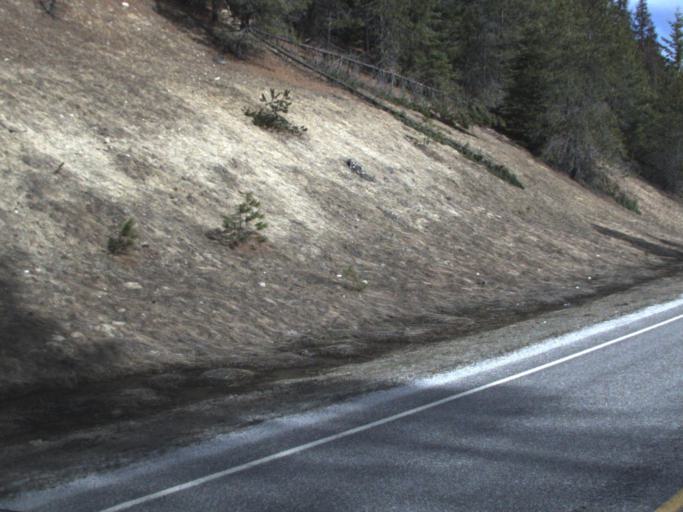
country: US
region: Washington
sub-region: Pend Oreille County
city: Newport
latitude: 48.3974
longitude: -117.3134
